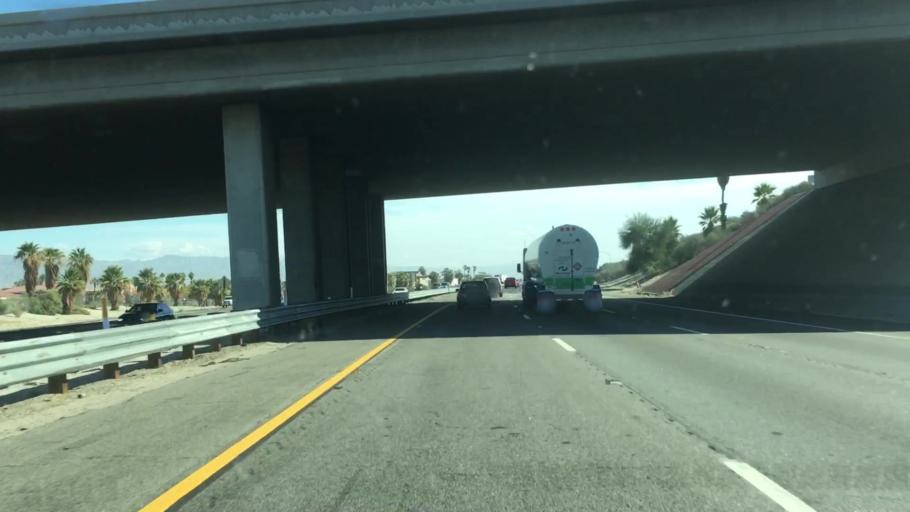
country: US
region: California
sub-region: Riverside County
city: Bermuda Dunes
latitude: 33.7605
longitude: -116.3017
